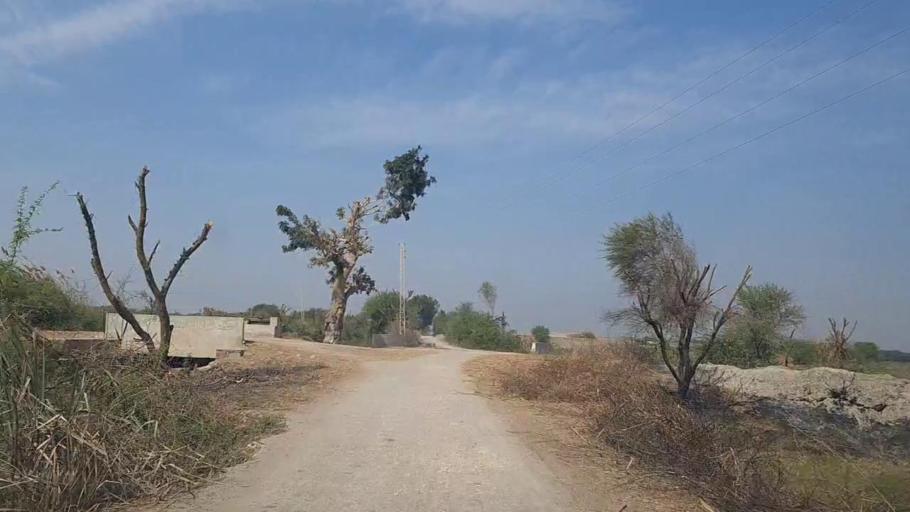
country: PK
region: Sindh
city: Mirpur Khas
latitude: 25.4861
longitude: 68.9256
